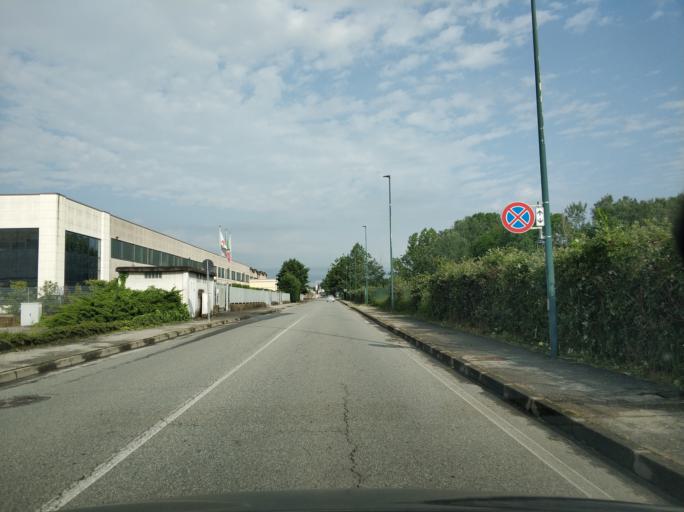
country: IT
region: Piedmont
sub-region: Provincia di Torino
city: Settimo Torinese
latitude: 45.1234
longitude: 7.7583
